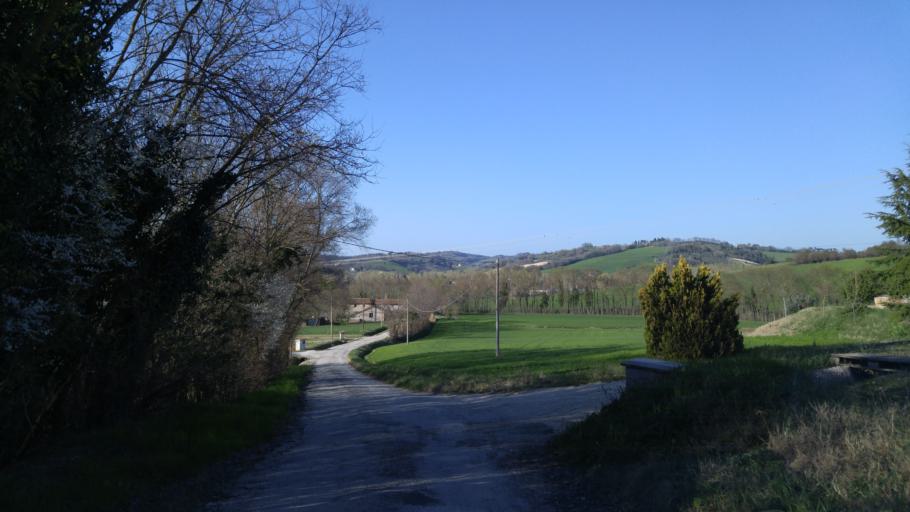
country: IT
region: The Marches
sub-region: Provincia di Pesaro e Urbino
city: Cuccurano
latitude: 43.8223
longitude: 12.9155
